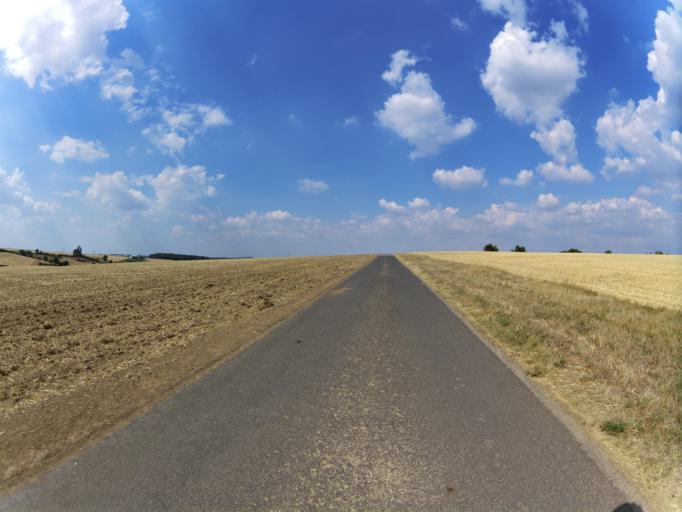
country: DE
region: Bavaria
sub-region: Regierungsbezirk Unterfranken
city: Ochsenfurt
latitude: 49.6464
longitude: 10.0652
